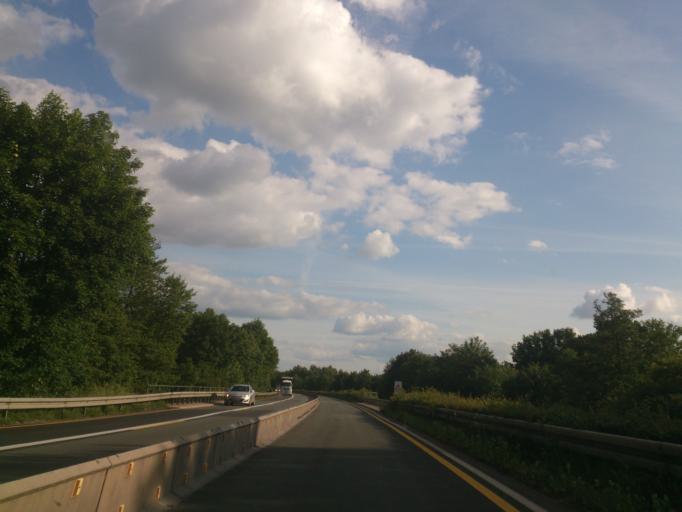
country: DE
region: North Rhine-Westphalia
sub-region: Regierungsbezirk Detmold
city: Hovelhof
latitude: 51.8090
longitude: 8.6986
